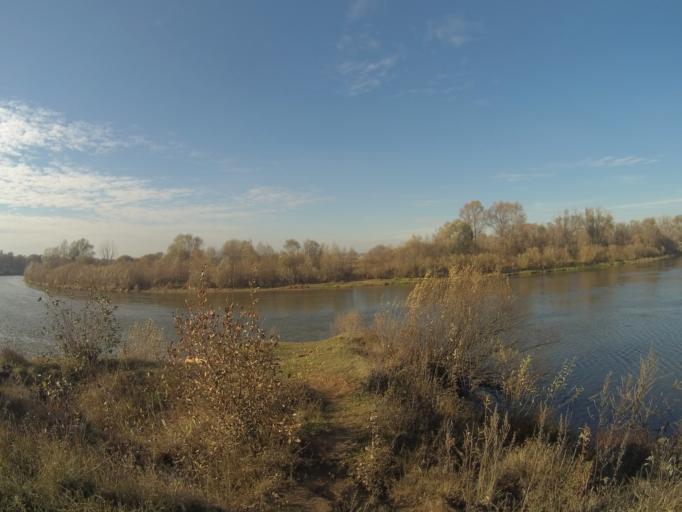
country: RU
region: Vladimir
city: Bogolyubovo
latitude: 56.1845
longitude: 40.5650
